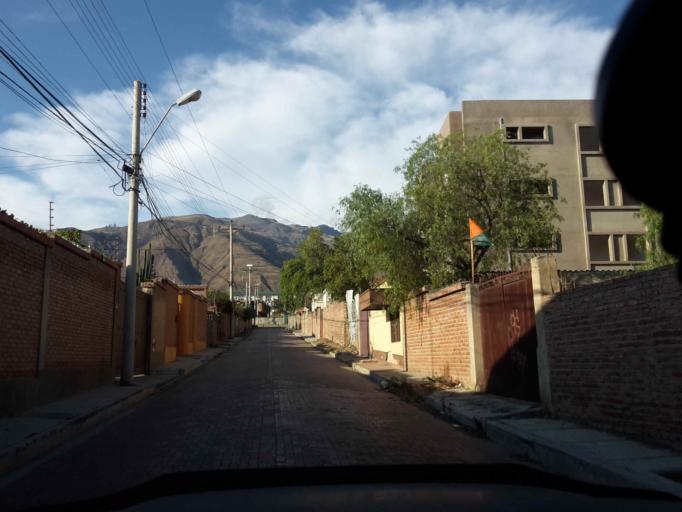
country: BO
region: Cochabamba
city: Cochabamba
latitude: -17.3482
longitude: -66.1940
